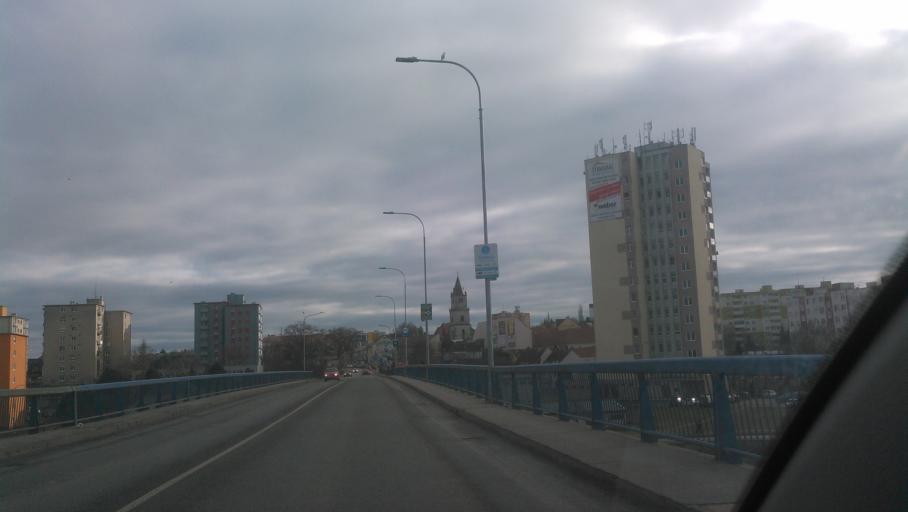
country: SK
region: Trnavsky
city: Hlohovec
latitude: 48.4298
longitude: 17.7923
